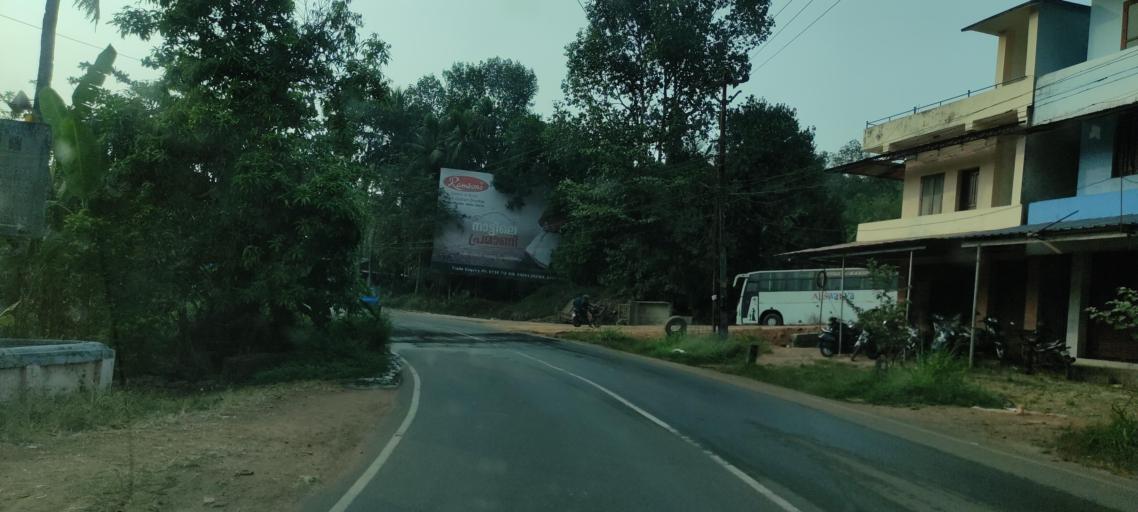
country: IN
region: Kerala
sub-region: Pattanamtitta
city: Adur
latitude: 9.1655
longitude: 76.6870
